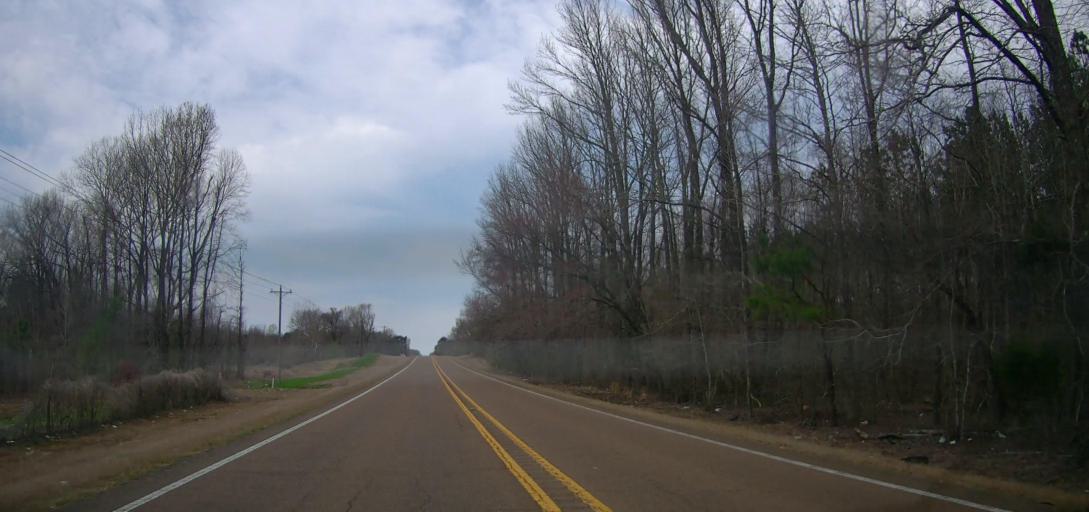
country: US
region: Mississippi
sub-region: Marshall County
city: Byhalia
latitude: 34.8516
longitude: -89.6338
